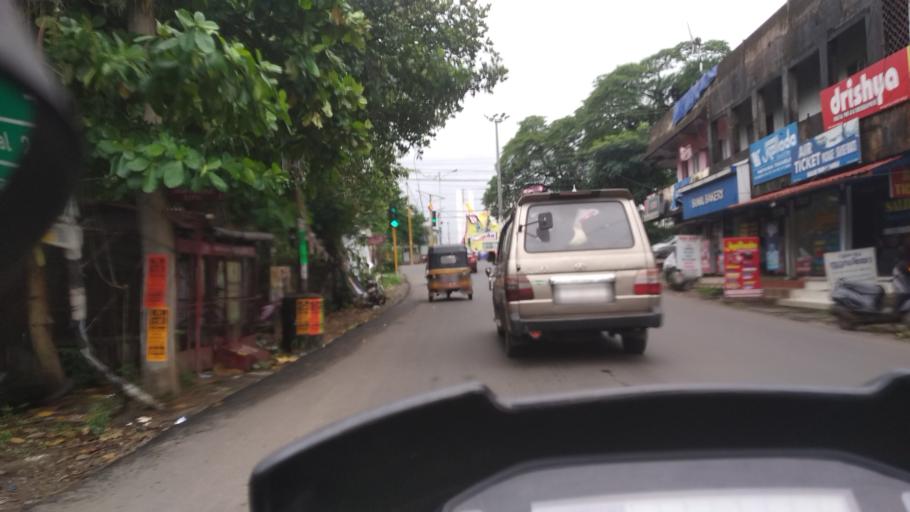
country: IN
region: Kerala
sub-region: Alappuzha
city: Alleppey
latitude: 9.5000
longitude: 76.3387
